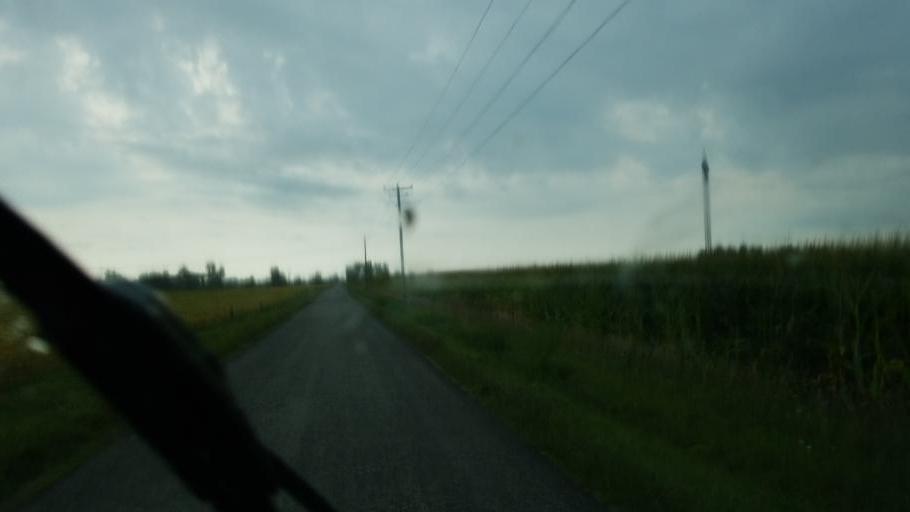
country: US
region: Ohio
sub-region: Crawford County
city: Galion
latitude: 40.7089
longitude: -82.8493
